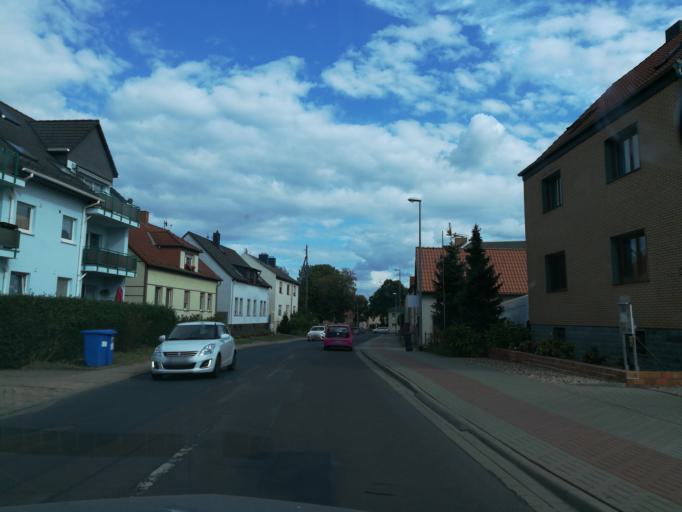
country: DE
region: Saxony-Anhalt
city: Diesdorf
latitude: 52.1307
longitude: 11.5620
